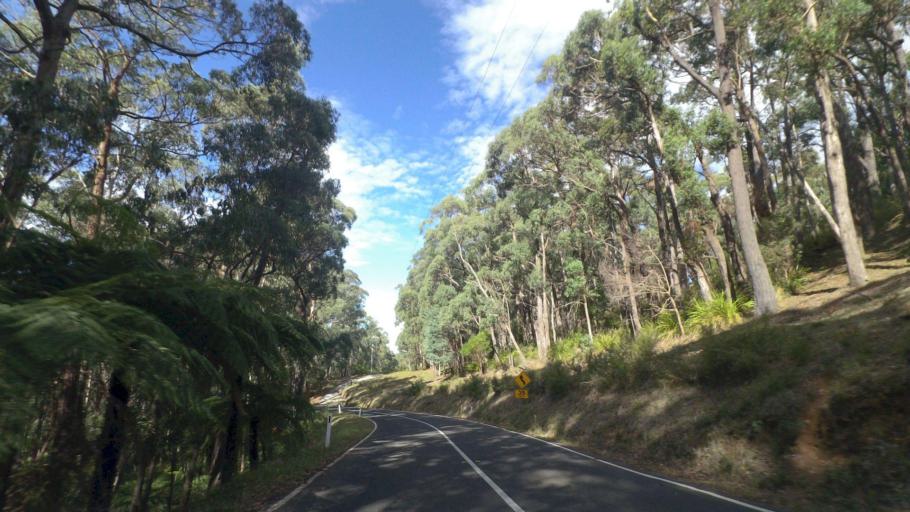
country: AU
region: Victoria
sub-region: Cardinia
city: Gembrook
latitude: -37.9746
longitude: 145.5793
